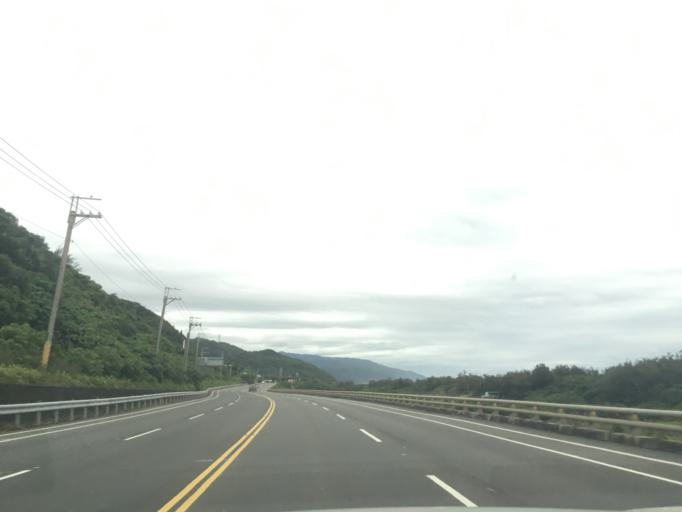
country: TW
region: Taiwan
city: Hengchun
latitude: 22.2974
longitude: 120.8888
